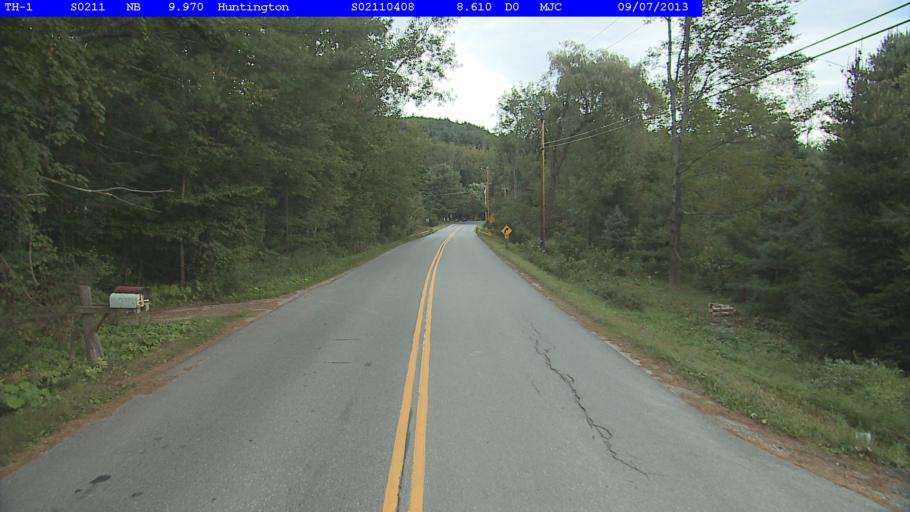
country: US
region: Vermont
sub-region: Chittenden County
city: Hinesburg
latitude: 44.3393
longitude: -72.9980
